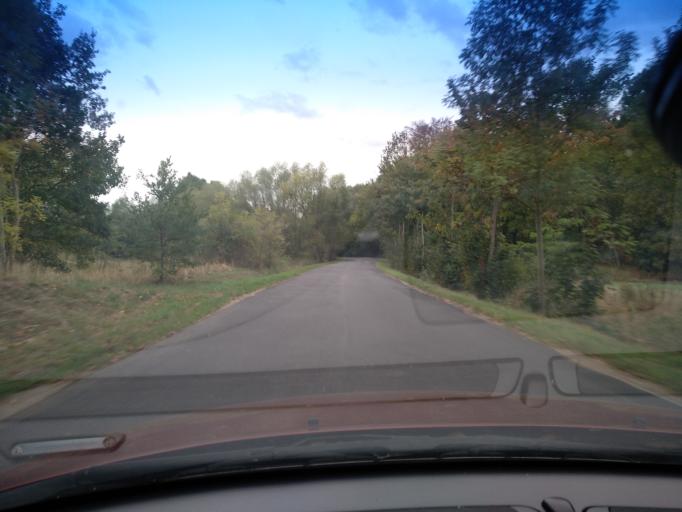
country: PL
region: Lower Silesian Voivodeship
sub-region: Powiat zgorzelecki
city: Zgorzelec
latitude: 51.1721
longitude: 15.0091
